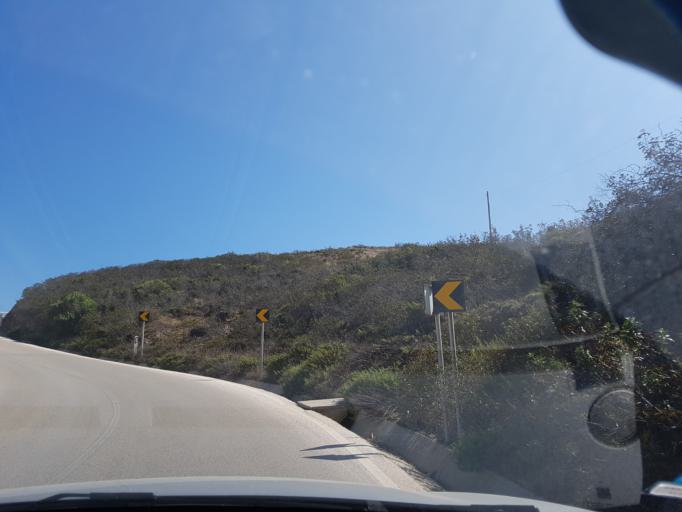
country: PT
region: Faro
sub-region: Vila do Bispo
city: Vila do Bispo
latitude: 37.0994
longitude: -8.9367
